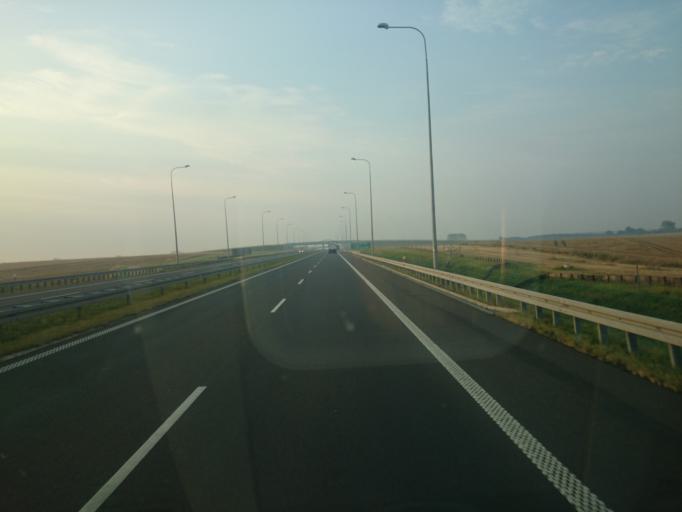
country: PL
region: West Pomeranian Voivodeship
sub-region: Powiat pyrzycki
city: Bielice
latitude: 53.1292
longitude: 14.7309
